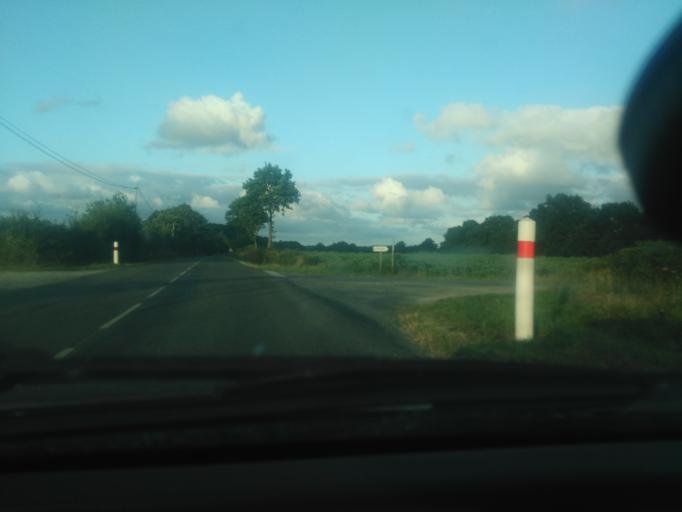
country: FR
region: Pays de la Loire
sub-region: Departement de la Vendee
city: La Ferriere
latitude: 46.7125
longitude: -1.3006
